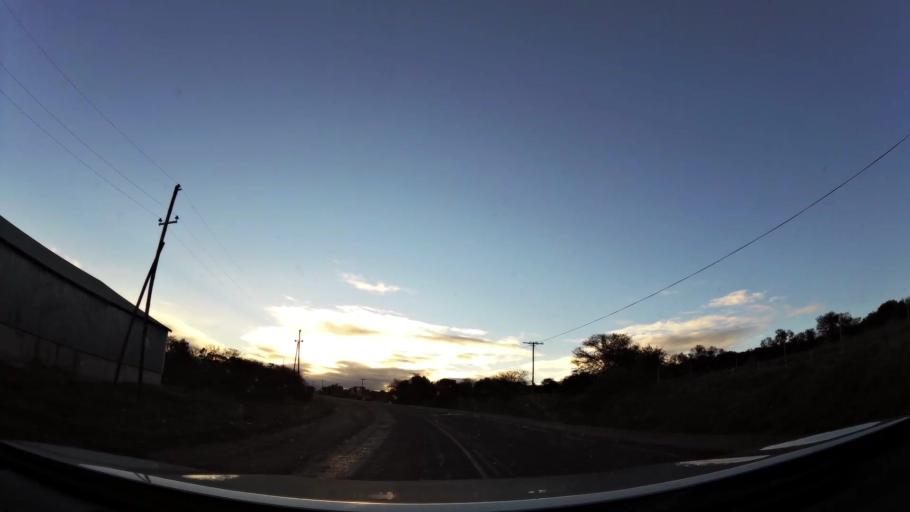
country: ZA
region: Western Cape
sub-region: Eden District Municipality
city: Riversdale
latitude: -34.0826
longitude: 20.9455
